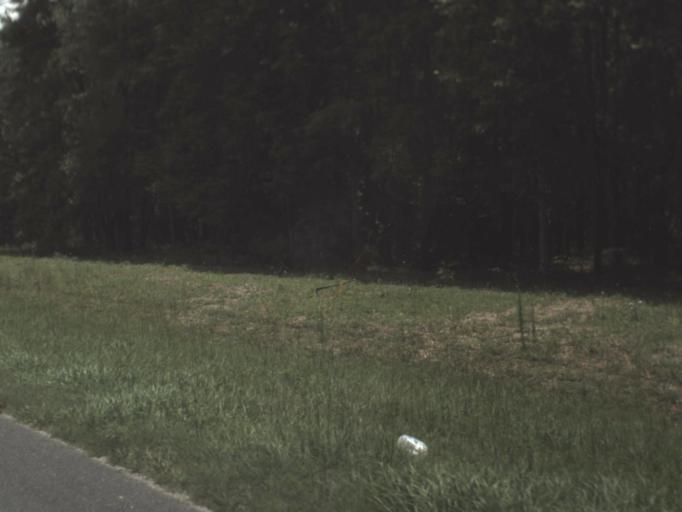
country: US
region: Florida
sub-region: Levy County
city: Manatee Road
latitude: 29.6028
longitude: -82.9234
